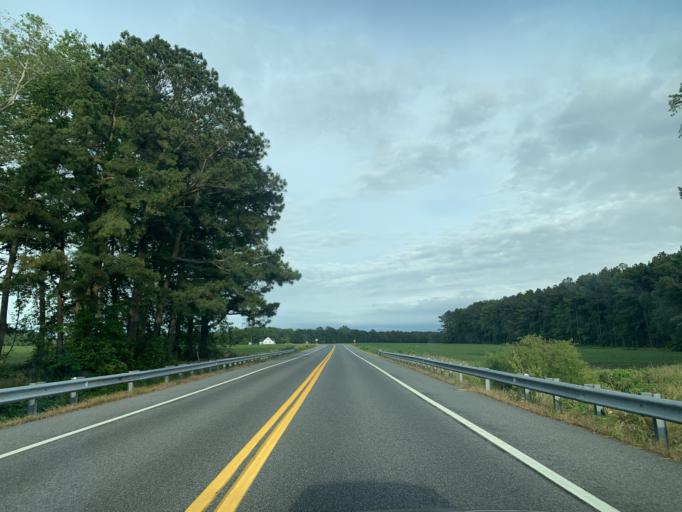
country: US
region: Virginia
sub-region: Accomack County
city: Captains Cove
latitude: 38.0686
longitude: -75.4389
